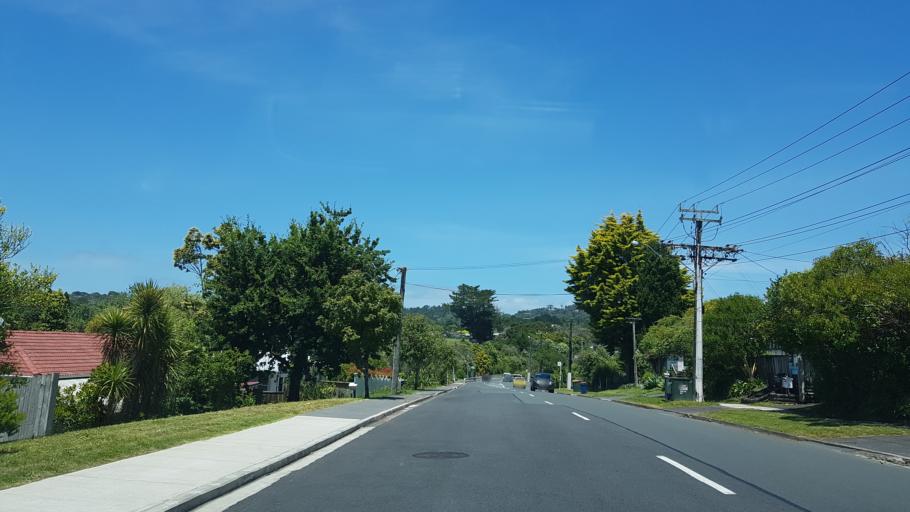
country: NZ
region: Auckland
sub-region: Auckland
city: Waitakere
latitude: -36.9181
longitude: 174.6493
